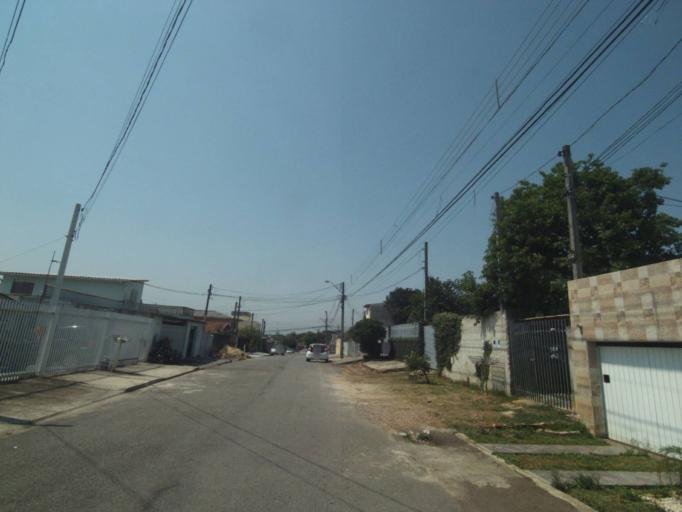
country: BR
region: Parana
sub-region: Sao Jose Dos Pinhais
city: Sao Jose dos Pinhais
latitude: -25.5143
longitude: -49.2797
